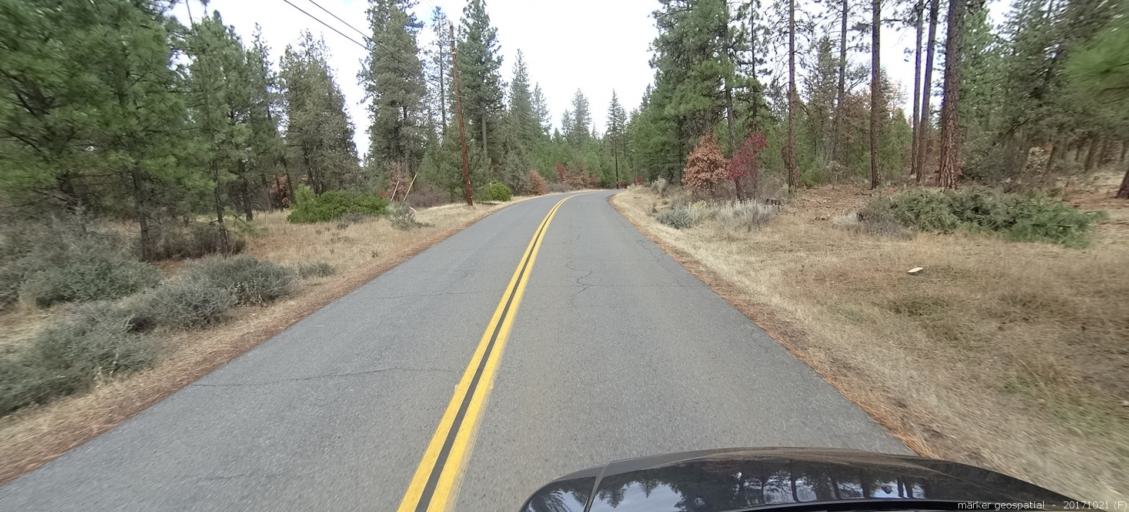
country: US
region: California
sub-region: Shasta County
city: Burney
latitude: 40.9289
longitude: -121.6449
